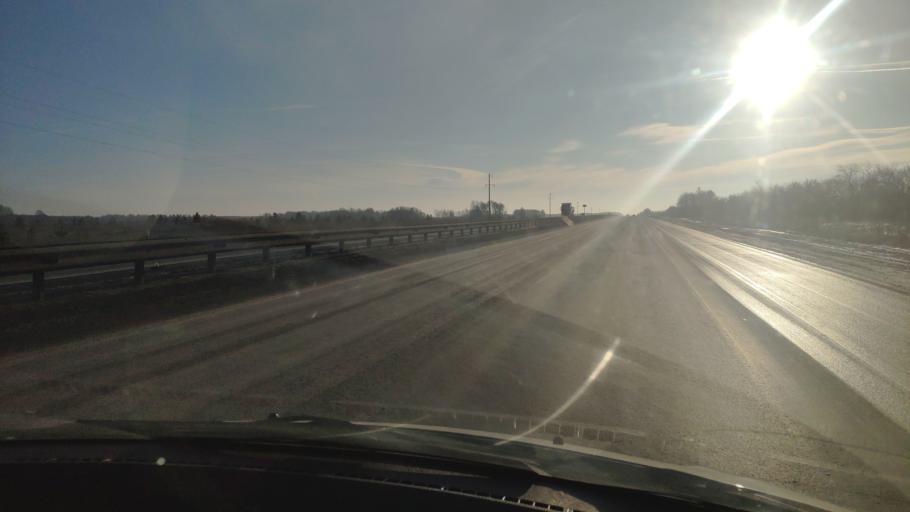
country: RU
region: Chelyabinsk
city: Kunashak
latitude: 55.7436
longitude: 61.2276
